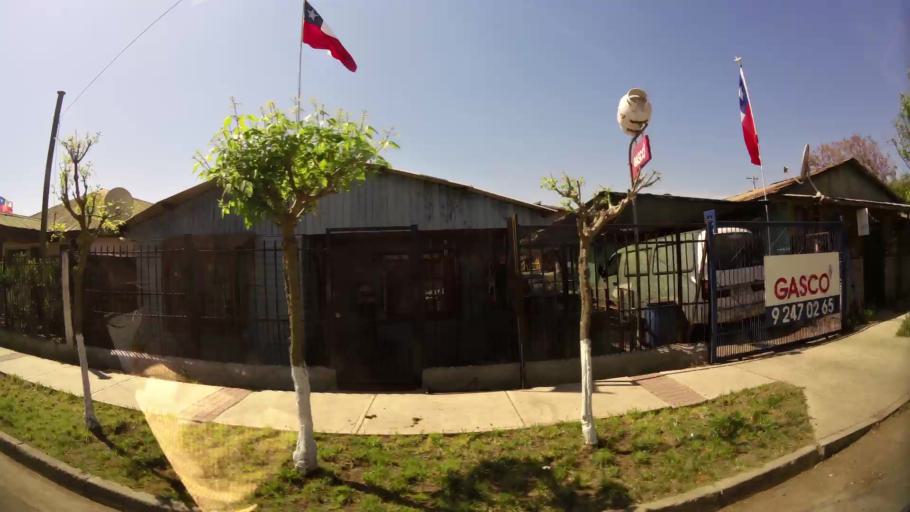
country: CL
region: Santiago Metropolitan
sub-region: Provincia de Talagante
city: Talagante
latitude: -33.6517
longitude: -70.9261
